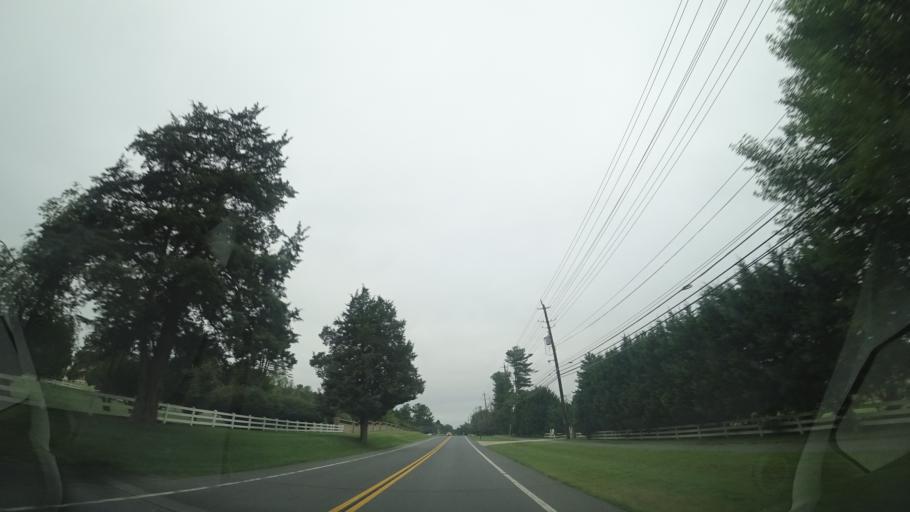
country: US
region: Maryland
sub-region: Montgomery County
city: Potomac
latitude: 39.0042
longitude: -77.1859
